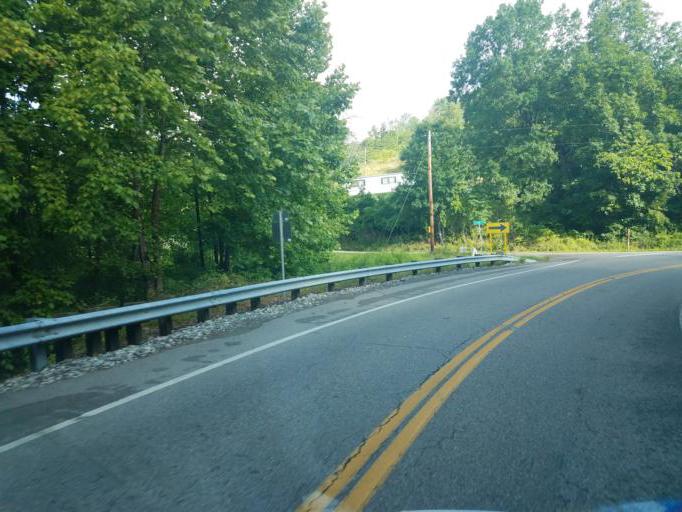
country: US
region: Ohio
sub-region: Gallia County
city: Gallipolis
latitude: 38.7740
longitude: -82.3579
